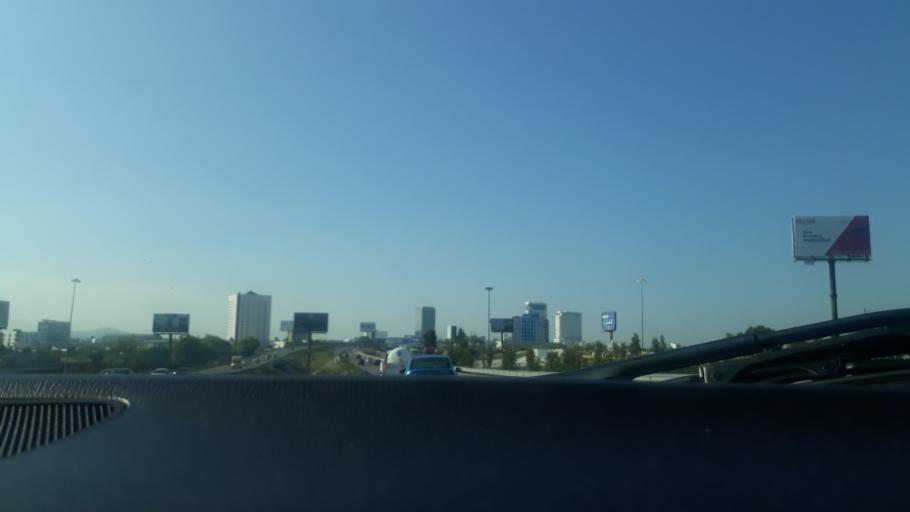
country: MX
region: Puebla
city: Tlazcalancingo
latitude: 19.0086
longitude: -98.2607
